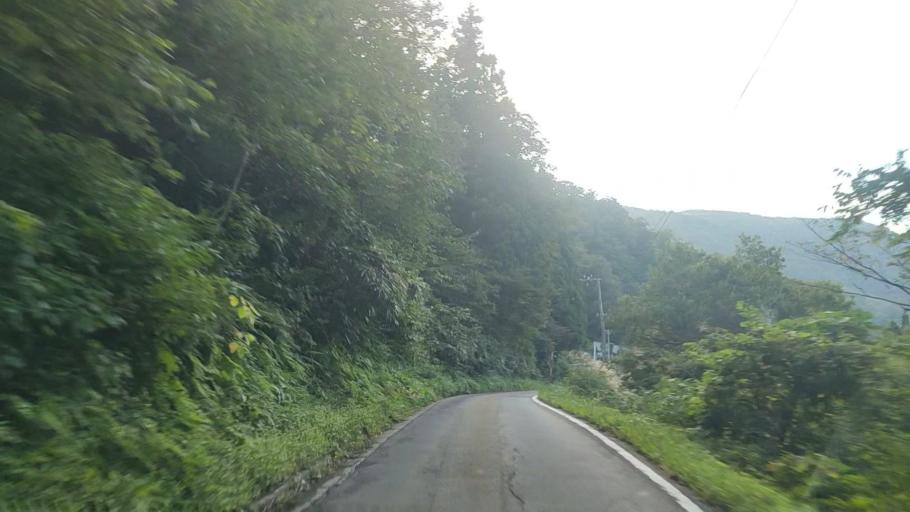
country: JP
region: Toyama
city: Yatsuomachi-higashikumisaka
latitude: 36.4833
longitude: 137.0687
